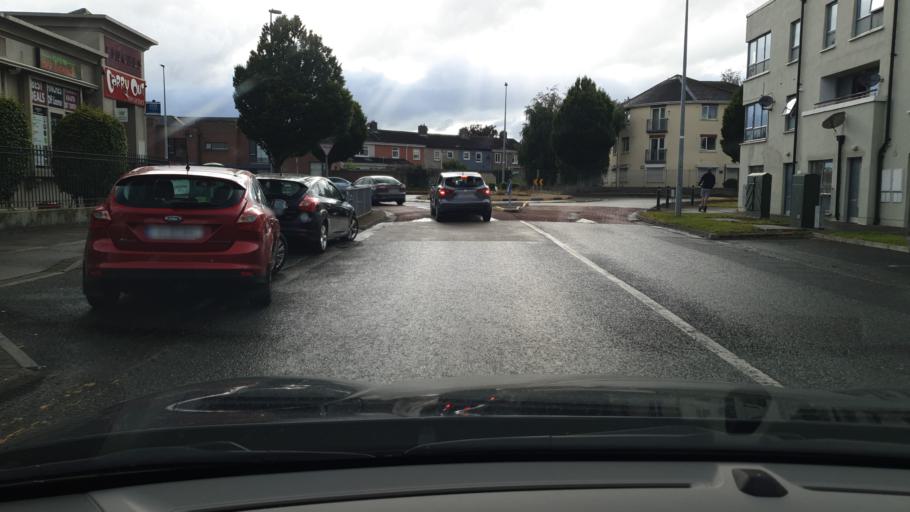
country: IE
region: Leinster
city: Clondalkin
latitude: 53.3450
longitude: -6.3977
